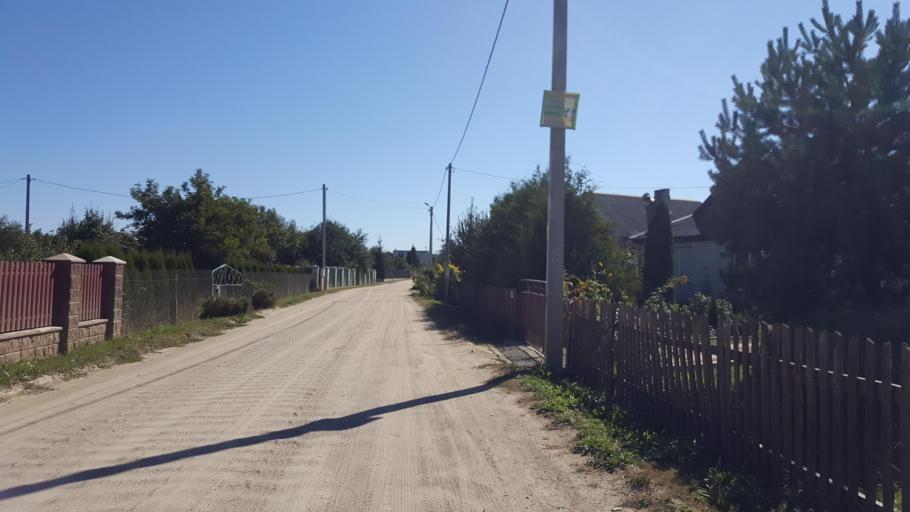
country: BY
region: Brest
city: Vysokaye
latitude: 52.2523
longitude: 23.4948
